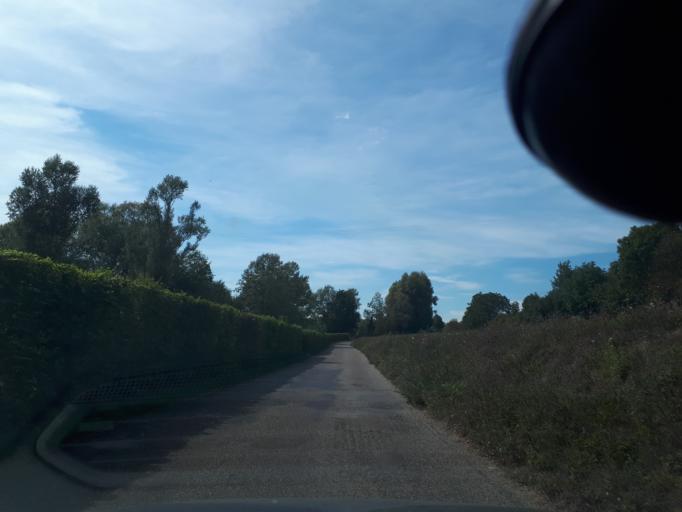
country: FR
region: Rhone-Alpes
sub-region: Departement de l'Isere
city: Chatonnay
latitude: 45.5078
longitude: 5.2090
